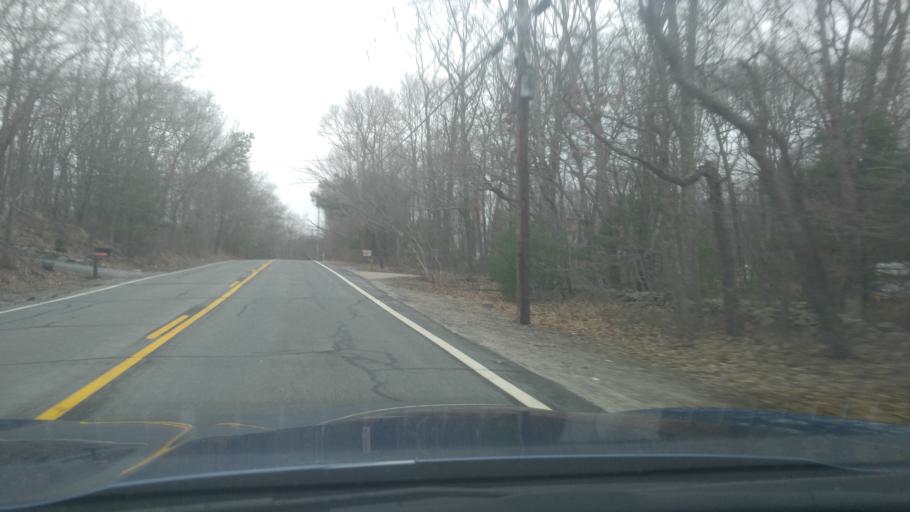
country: US
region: Rhode Island
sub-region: Kent County
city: Coventry
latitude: 41.6781
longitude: -71.6574
